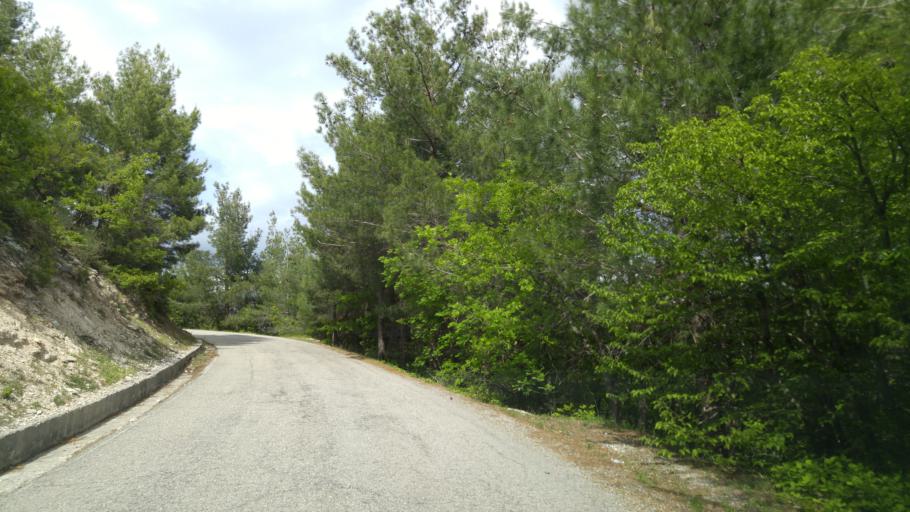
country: IT
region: The Marches
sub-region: Provincia di Pesaro e Urbino
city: Canavaccio
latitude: 43.7153
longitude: 12.7046
